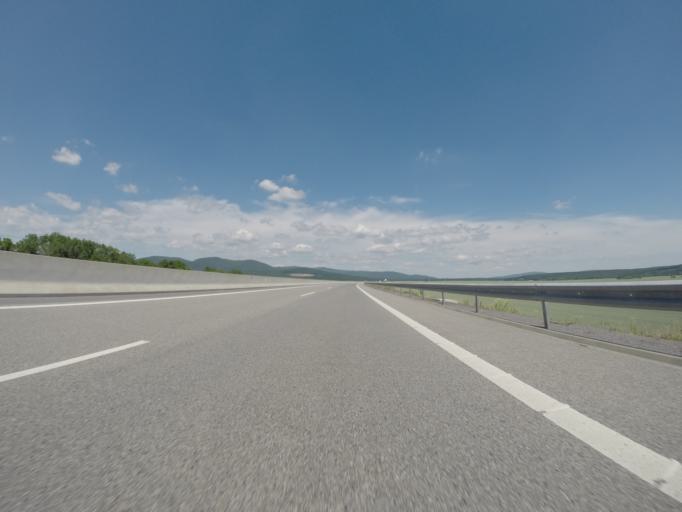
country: SK
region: Nitriansky
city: Zlate Moravce
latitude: 48.3507
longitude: 18.4402
